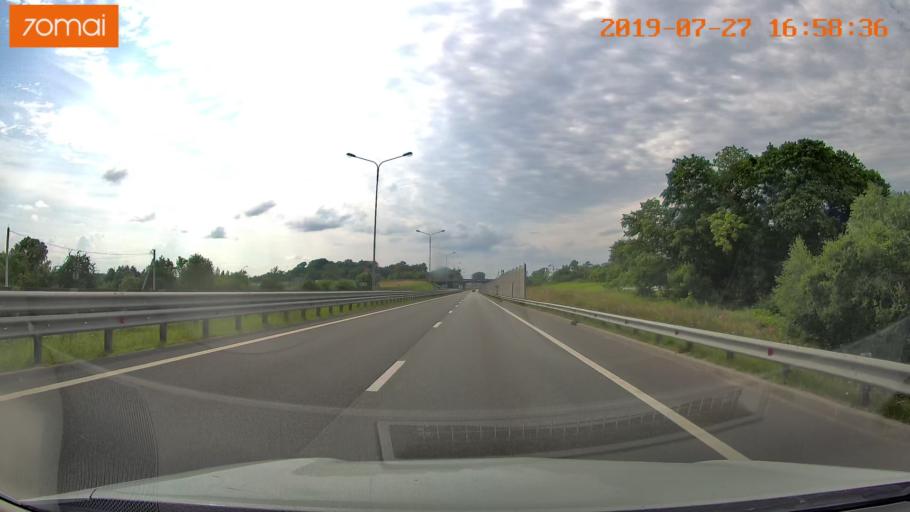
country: RU
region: Kaliningrad
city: Bol'shoe Isakovo
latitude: 54.7012
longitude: 20.6761
